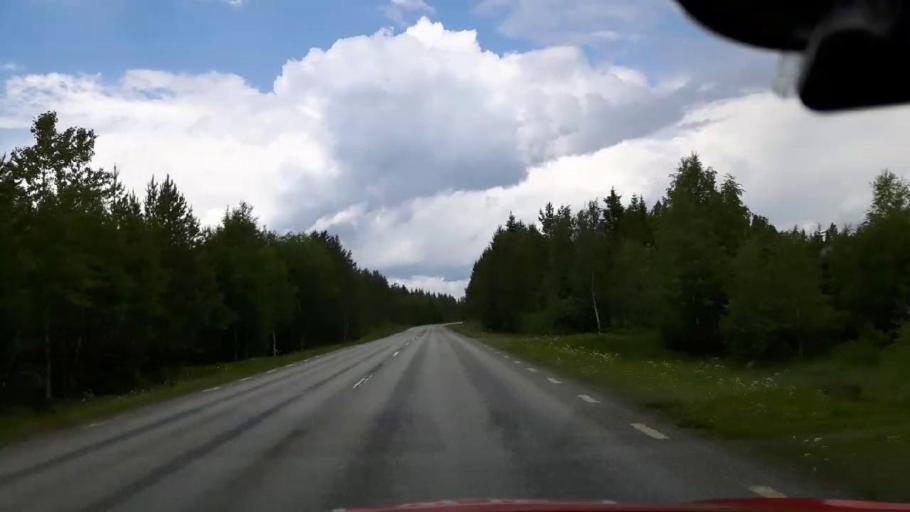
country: SE
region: Jaemtland
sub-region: Krokoms Kommun
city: Krokom
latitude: 63.3574
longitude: 14.4110
